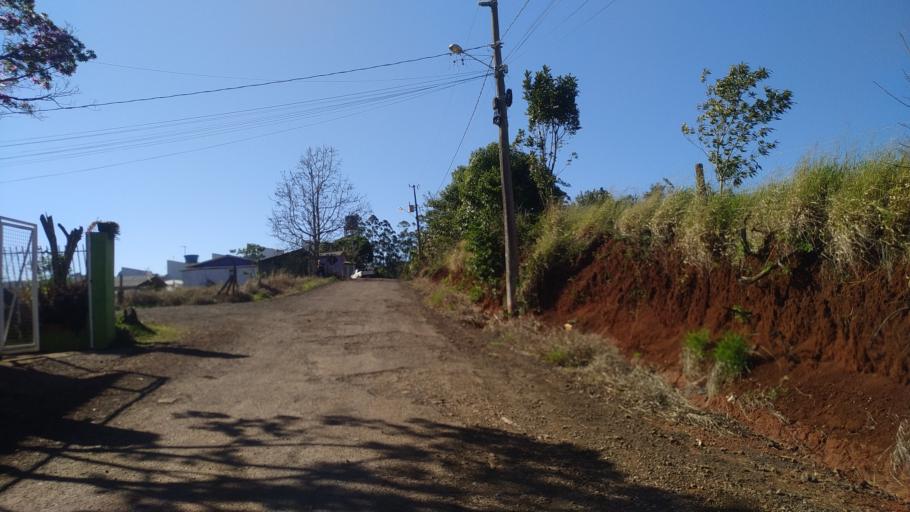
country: BR
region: Santa Catarina
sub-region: Chapeco
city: Chapeco
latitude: -27.1497
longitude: -52.6136
